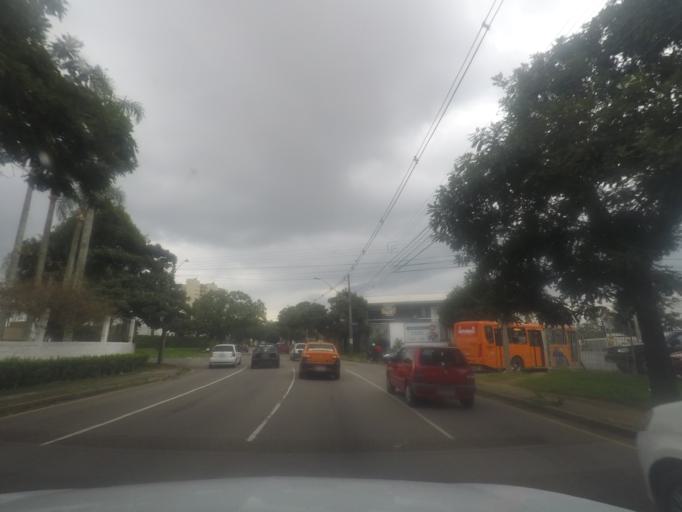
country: BR
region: Parana
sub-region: Curitiba
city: Curitiba
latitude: -25.4879
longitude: -49.2968
